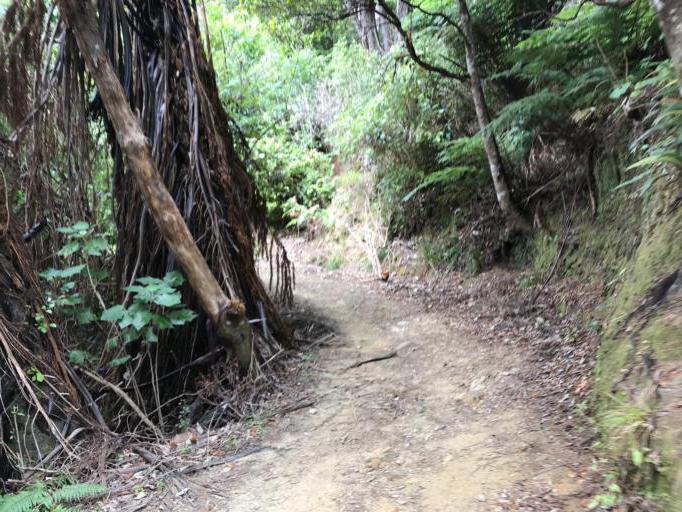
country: NZ
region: Marlborough
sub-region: Marlborough District
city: Picton
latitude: -41.1148
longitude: 174.2039
